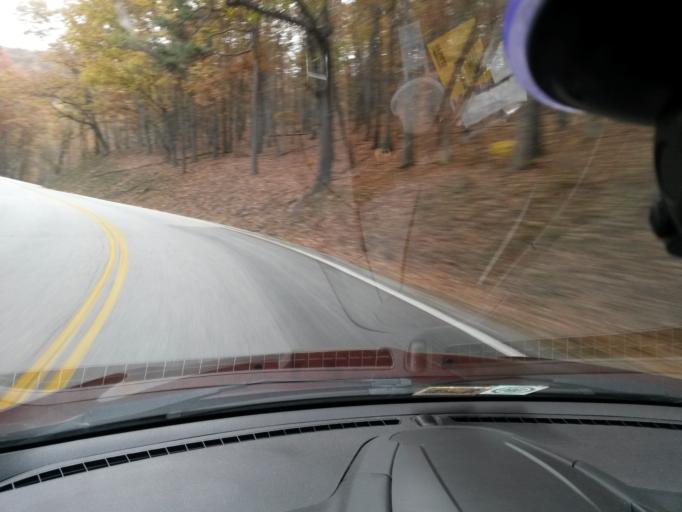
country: US
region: Virginia
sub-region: Rockbridge County
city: Glasgow
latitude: 37.6137
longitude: -79.4170
